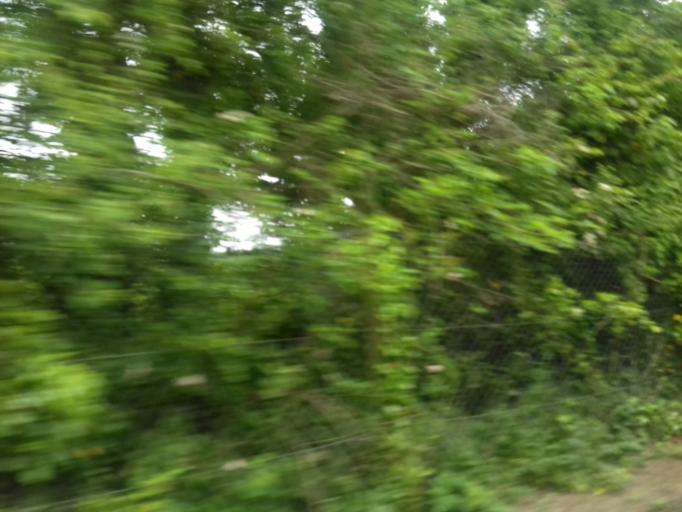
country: IE
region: Leinster
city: Donabate
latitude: 53.4887
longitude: -6.1783
